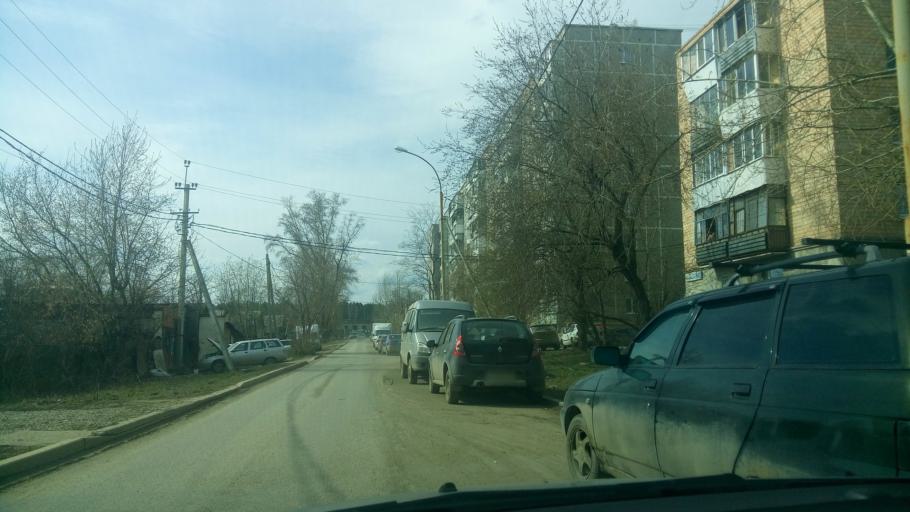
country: RU
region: Sverdlovsk
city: Verkhnyaya Pyshma
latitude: 56.9093
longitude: 60.5860
